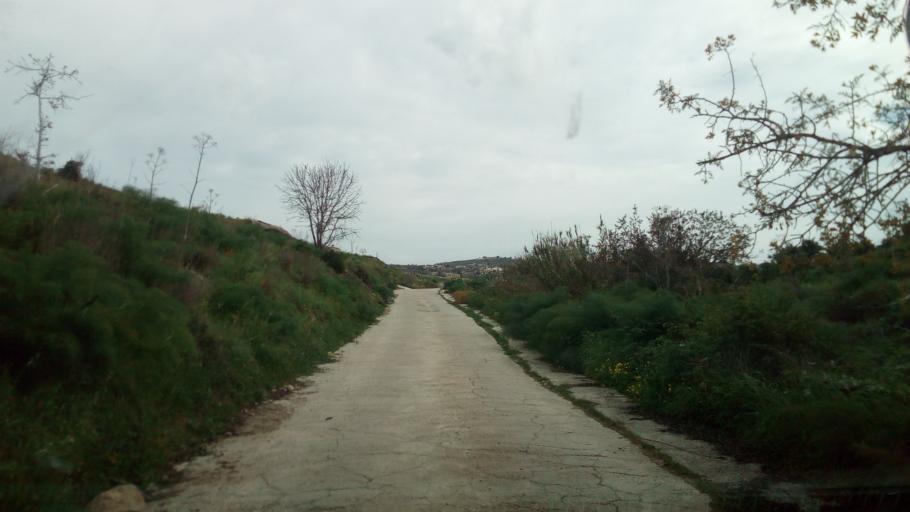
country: CY
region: Pafos
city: Mesogi
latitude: 34.7928
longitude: 32.4656
